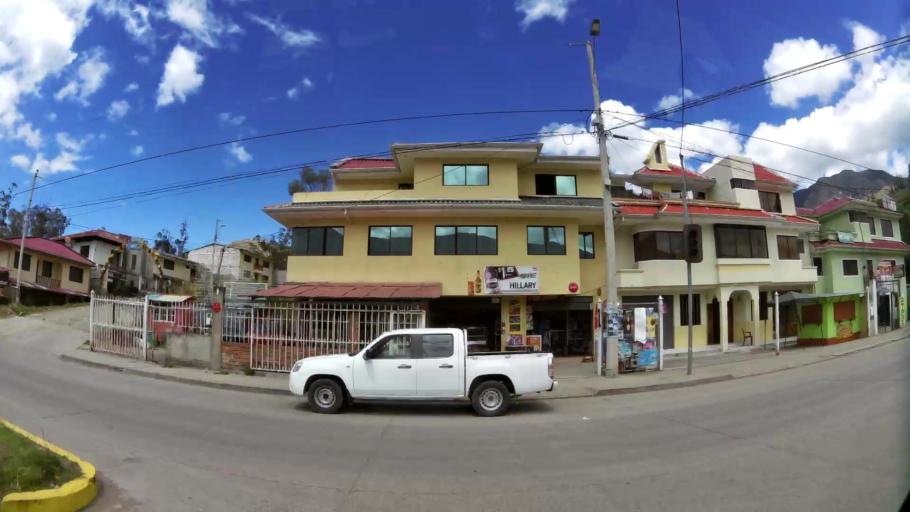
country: EC
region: Azuay
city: Cuenca
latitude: -3.1570
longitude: -79.1483
